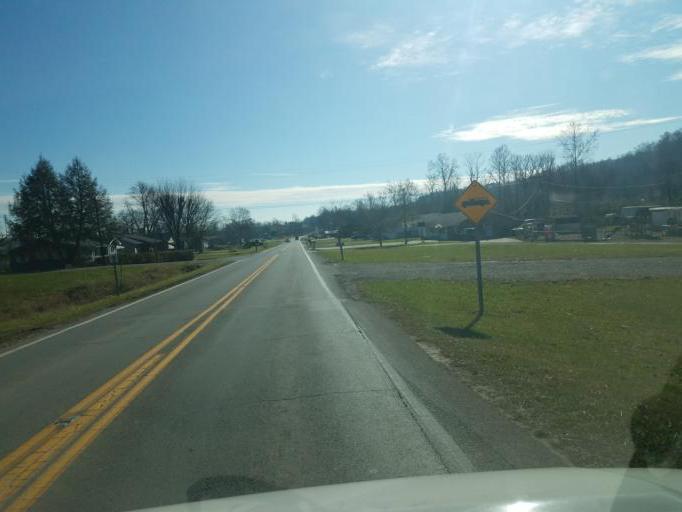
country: US
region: Ohio
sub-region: Scioto County
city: Sciotodale
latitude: 38.8567
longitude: -82.8574
